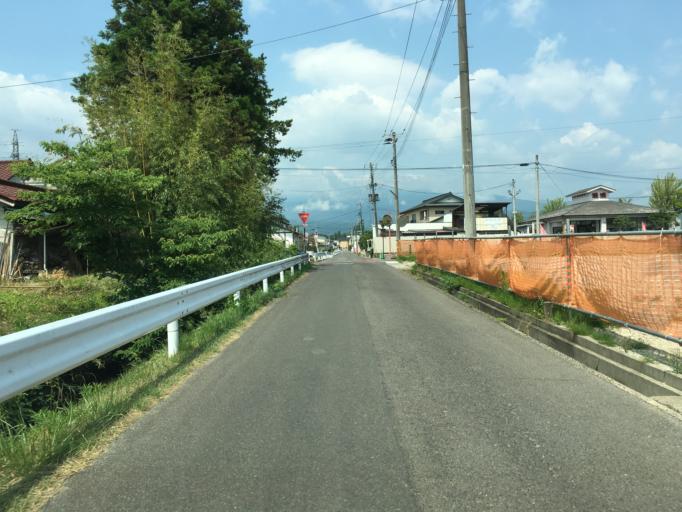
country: JP
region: Fukushima
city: Fukushima-shi
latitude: 37.7393
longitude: 140.4302
